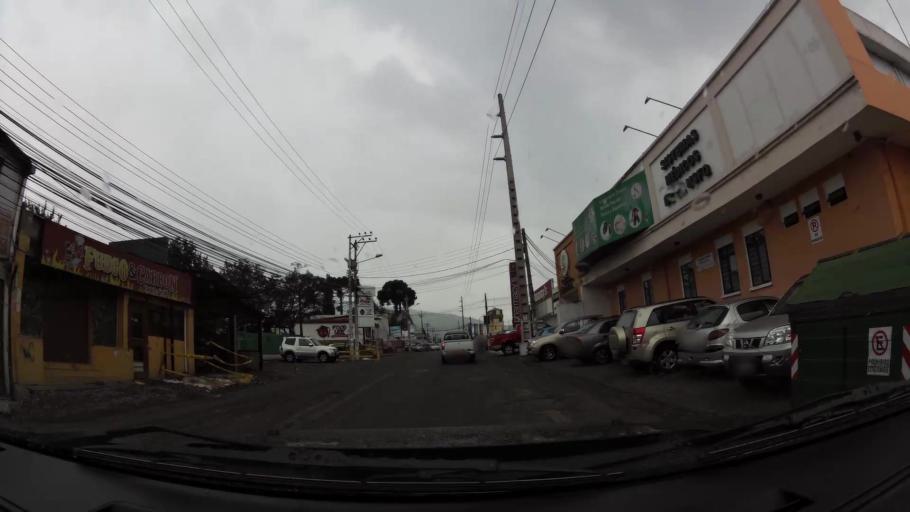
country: EC
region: Pichincha
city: Sangolqui
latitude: -0.3004
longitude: -78.4607
